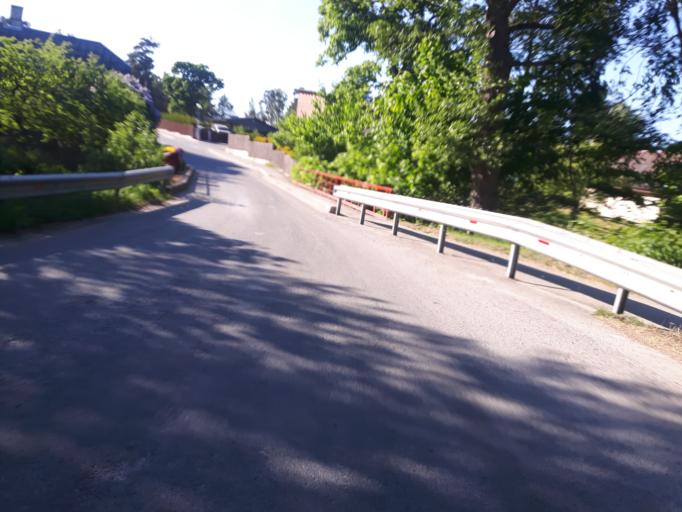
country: EE
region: Harju
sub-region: Loksa linn
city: Loksa
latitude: 59.5785
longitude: 25.9708
